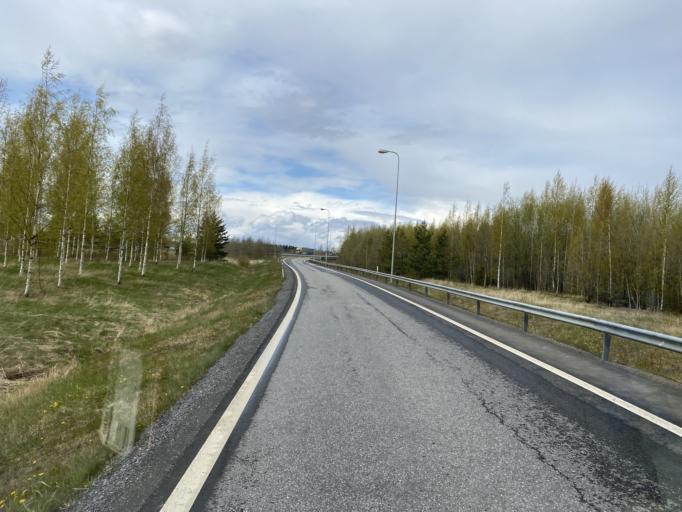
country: FI
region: Pirkanmaa
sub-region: Etelae-Pirkanmaa
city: Toijala
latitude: 61.2083
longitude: 23.8420
